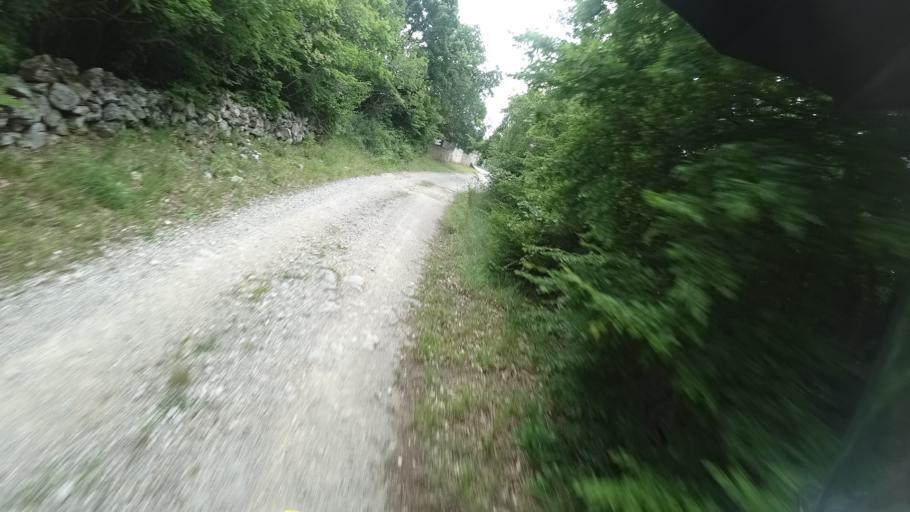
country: HR
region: Sibensko-Kniniska
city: Kistanje
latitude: 44.0908
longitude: 16.0374
